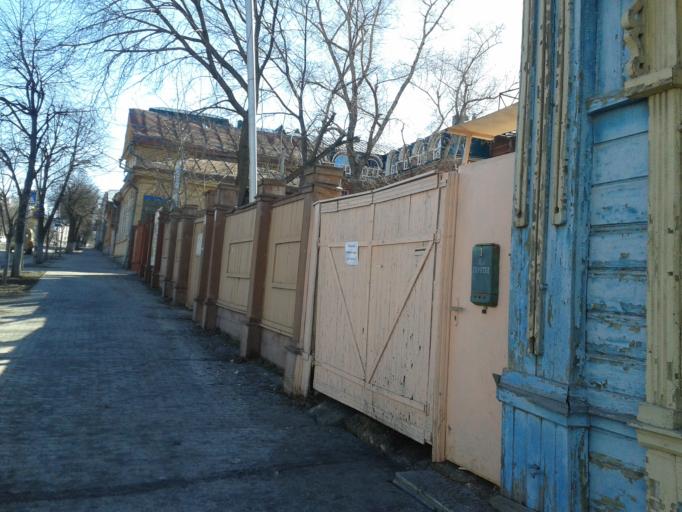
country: RU
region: Ulyanovsk
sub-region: Ulyanovskiy Rayon
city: Ulyanovsk
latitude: 54.3133
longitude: 48.3888
